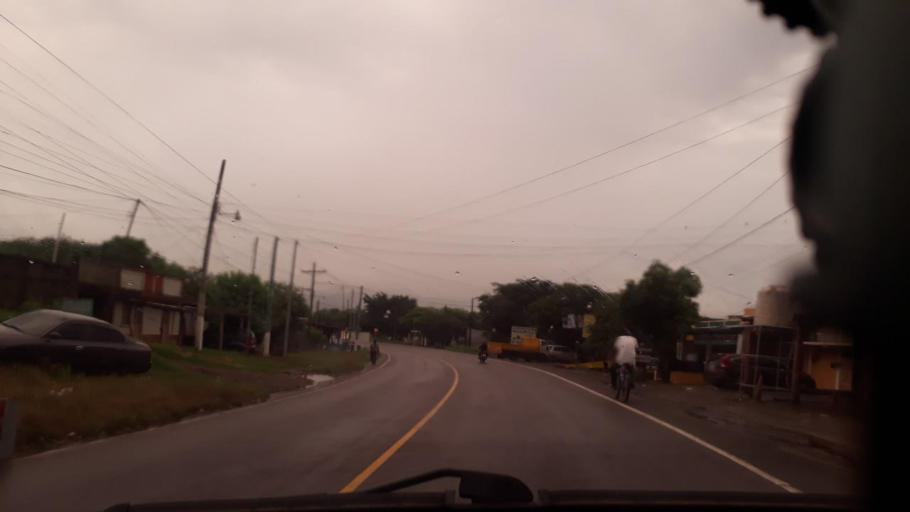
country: SV
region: Ahuachapan
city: San Francisco Menendez
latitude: 13.8796
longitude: -90.0973
